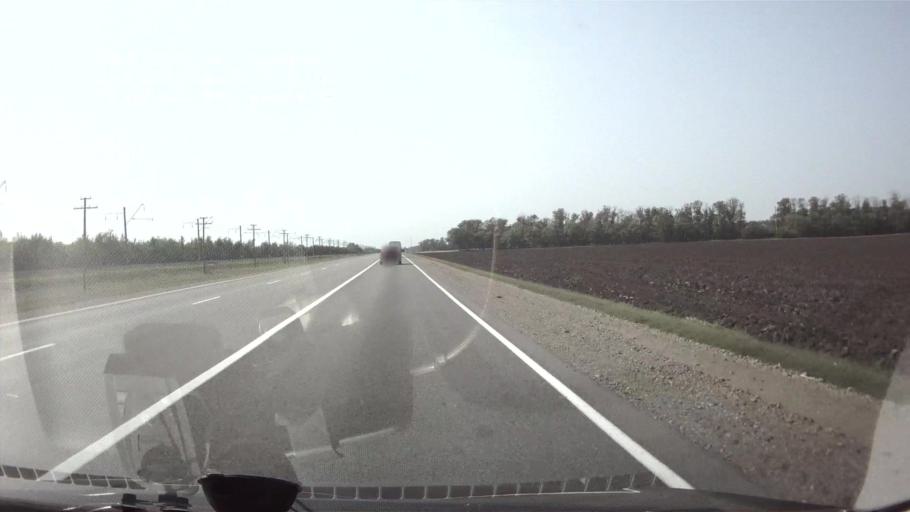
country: RU
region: Krasnodarskiy
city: Dvubratskiy
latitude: 45.2523
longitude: 39.7655
